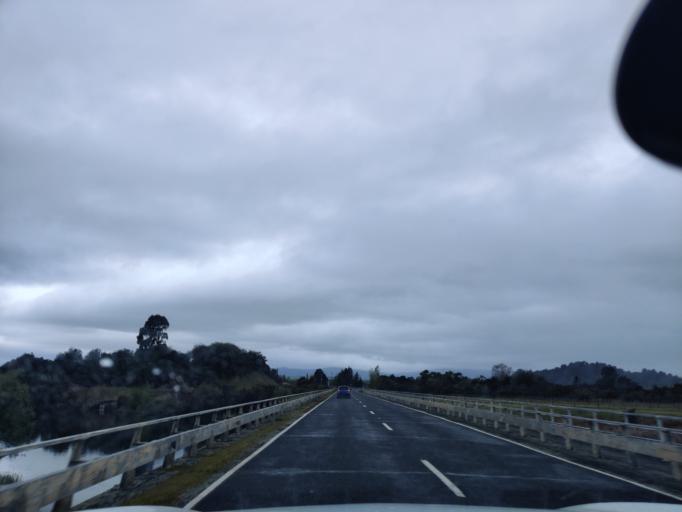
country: NZ
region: Waikato
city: Turangi
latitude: -38.9786
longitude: 175.7742
